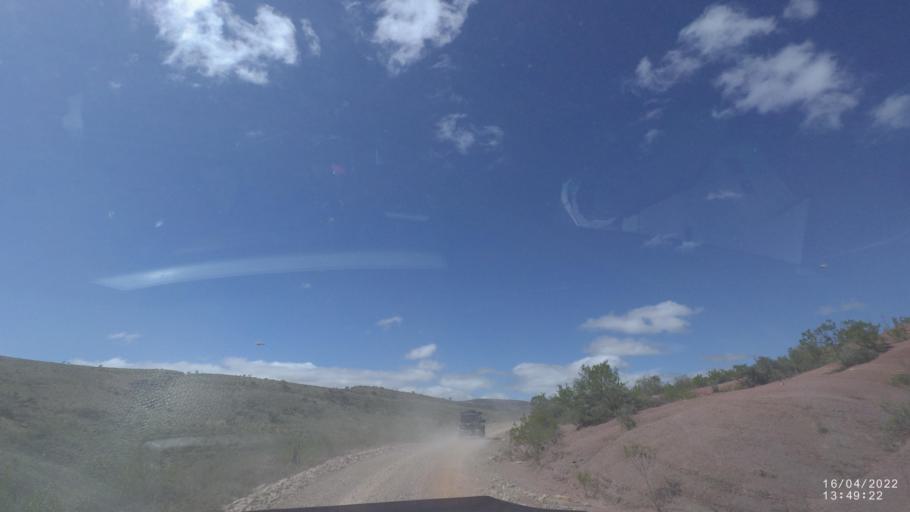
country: BO
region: Cochabamba
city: Mizque
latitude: -18.0130
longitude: -65.5778
